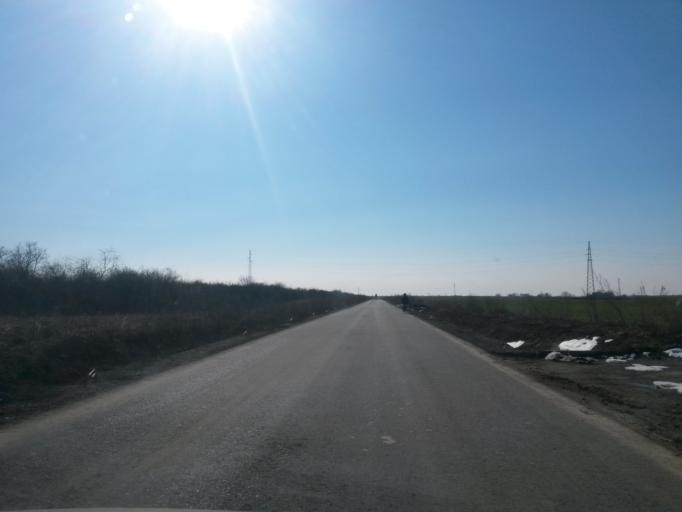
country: HR
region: Vukovarsko-Srijemska
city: Vukovar
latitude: 45.3217
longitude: 19.0025
